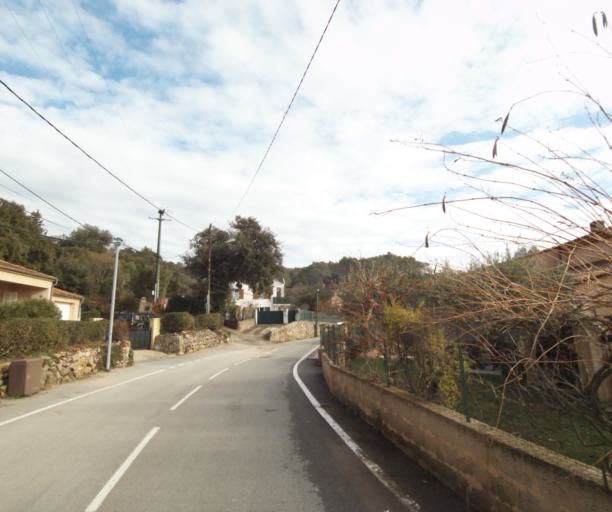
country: FR
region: Provence-Alpes-Cote d'Azur
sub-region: Departement du Var
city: Trans-en-Provence
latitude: 43.5032
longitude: 6.4932
